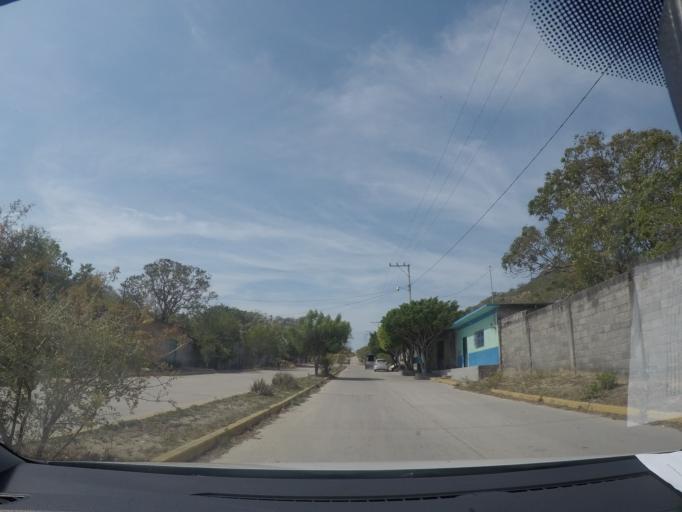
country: MX
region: Oaxaca
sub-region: Salina Cruz
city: Salina Cruz
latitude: 16.2183
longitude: -95.1259
